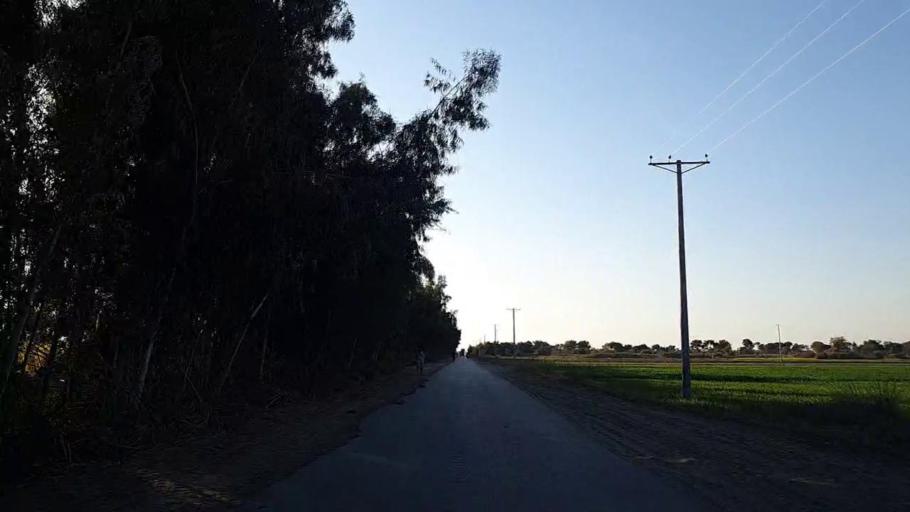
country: PK
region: Sindh
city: Sanghar
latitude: 26.2790
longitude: 68.9228
